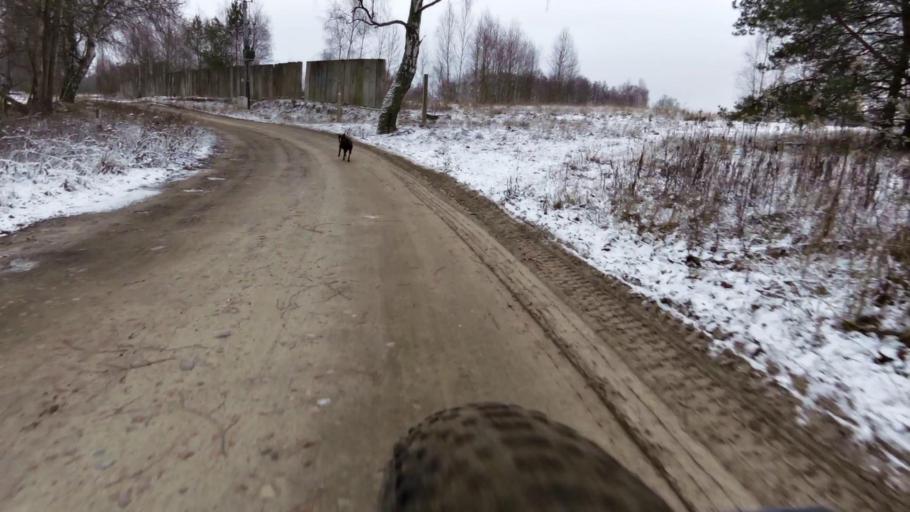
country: PL
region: West Pomeranian Voivodeship
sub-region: Powiat walecki
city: Miroslawiec
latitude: 53.3179
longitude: 16.0786
